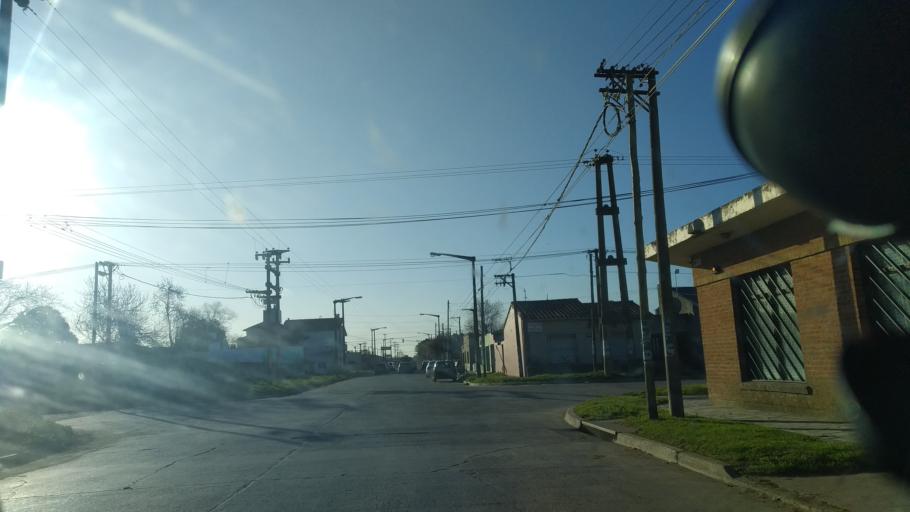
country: AR
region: Buenos Aires
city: Necochea
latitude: -38.5662
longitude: -58.7051
